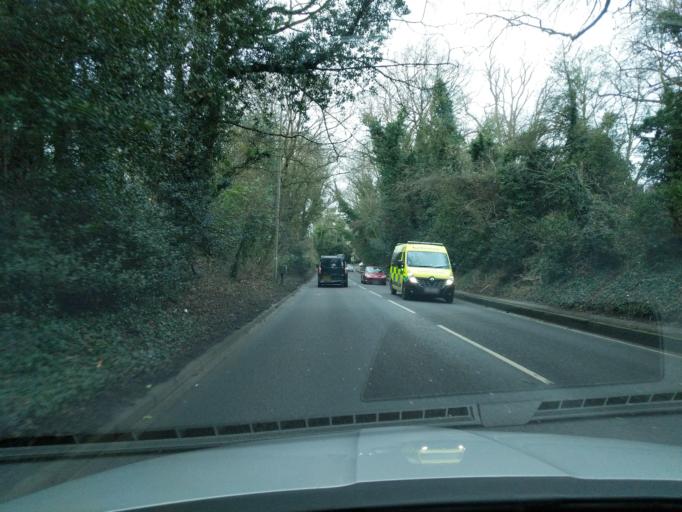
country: GB
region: England
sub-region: Hertfordshire
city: Abbots Langley
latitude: 51.6788
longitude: -0.4264
